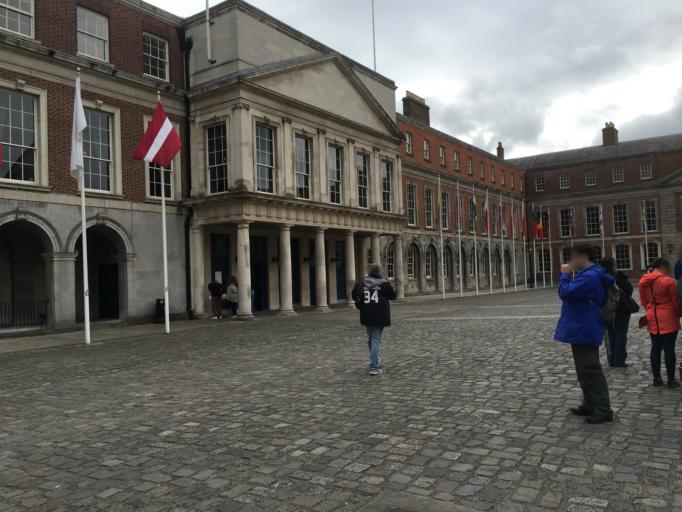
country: IE
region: Leinster
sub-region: Dublin City
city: Dublin
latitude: 53.3432
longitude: -6.2672
